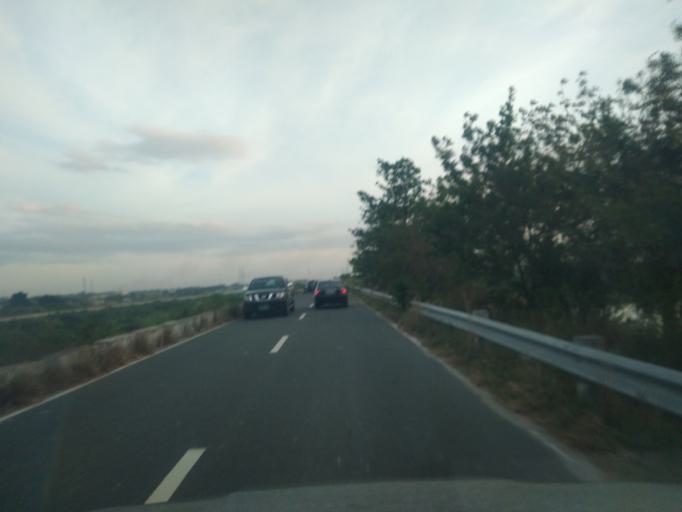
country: PH
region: Central Luzon
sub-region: Province of Pampanga
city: Santa Rita
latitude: 15.0067
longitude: 120.6309
